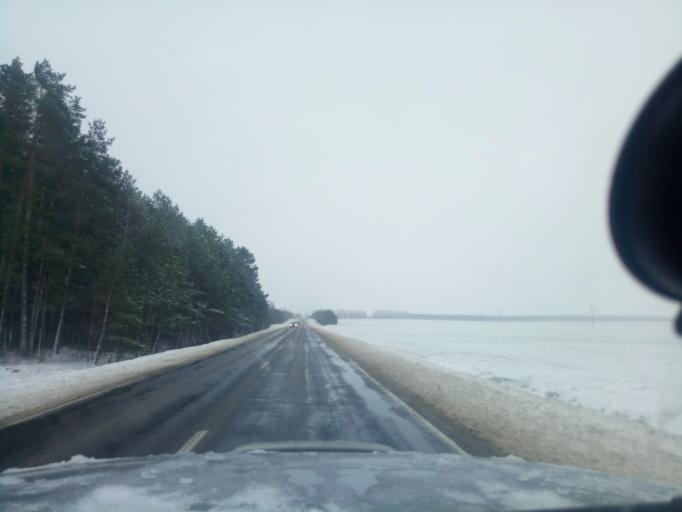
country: BY
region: Minsk
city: Haradzyeya
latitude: 53.3703
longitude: 26.5110
